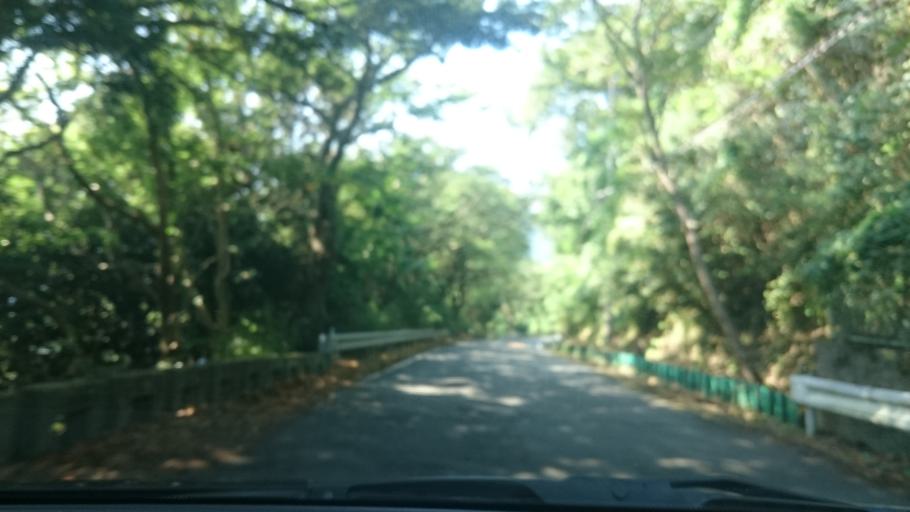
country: JP
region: Shizuoka
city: Heda
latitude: 34.9367
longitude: 138.7779
